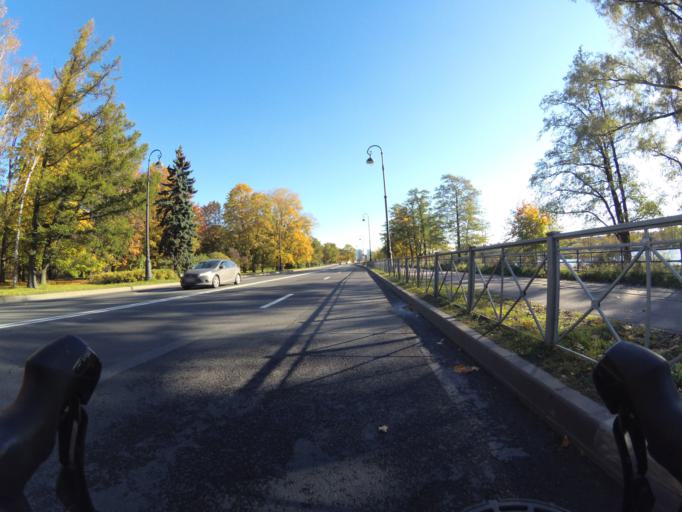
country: RU
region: Leningrad
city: Krestovskiy ostrov
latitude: 59.9670
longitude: 30.2512
